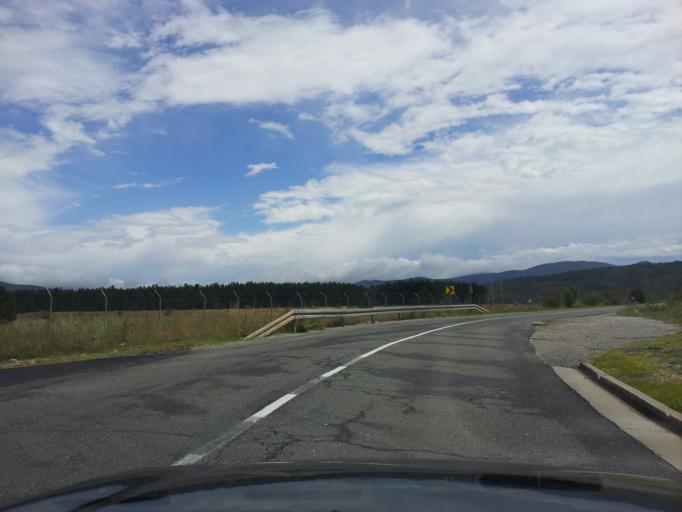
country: HR
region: Zadarska
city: Gracac
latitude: 44.5519
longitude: 15.7620
